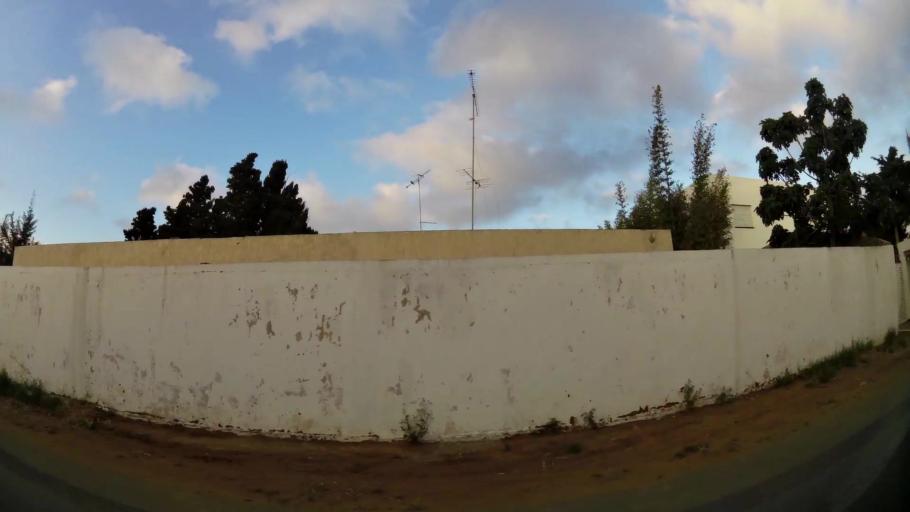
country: MA
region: Rabat-Sale-Zemmour-Zaer
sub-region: Rabat
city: Rabat
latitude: 33.9714
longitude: -6.8404
